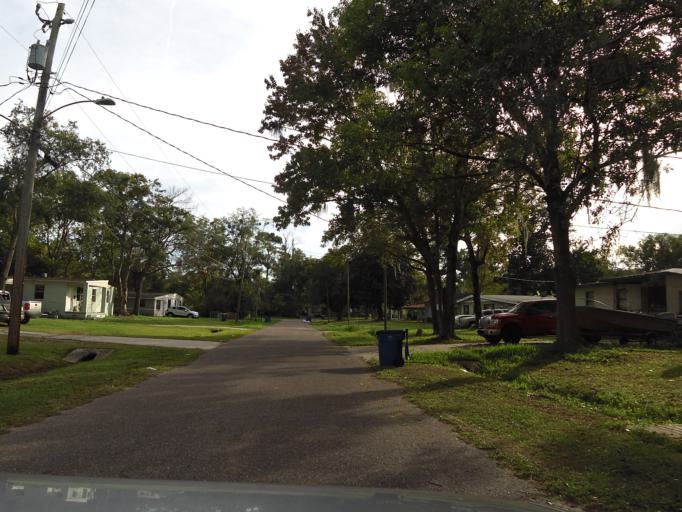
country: US
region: Florida
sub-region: Duval County
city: Jacksonville
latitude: 30.4265
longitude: -81.6750
